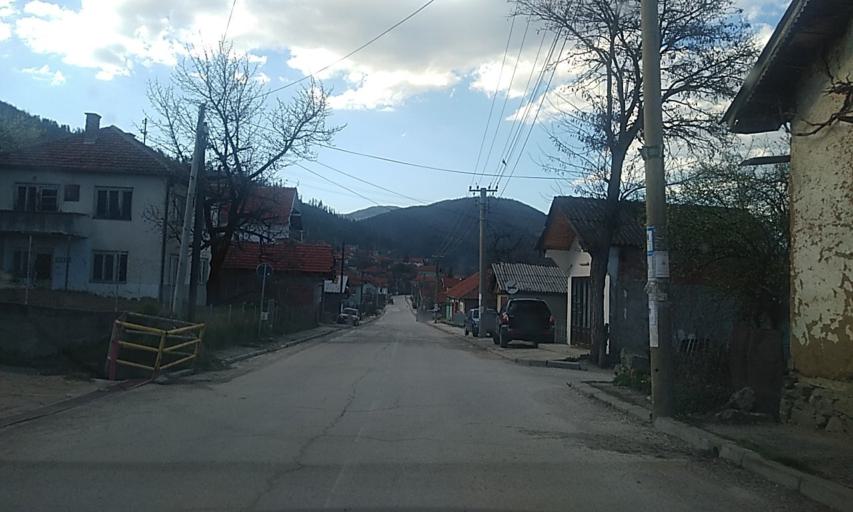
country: RS
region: Central Serbia
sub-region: Pcinjski Okrug
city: Bosilegrad
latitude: 42.4858
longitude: 22.4732
